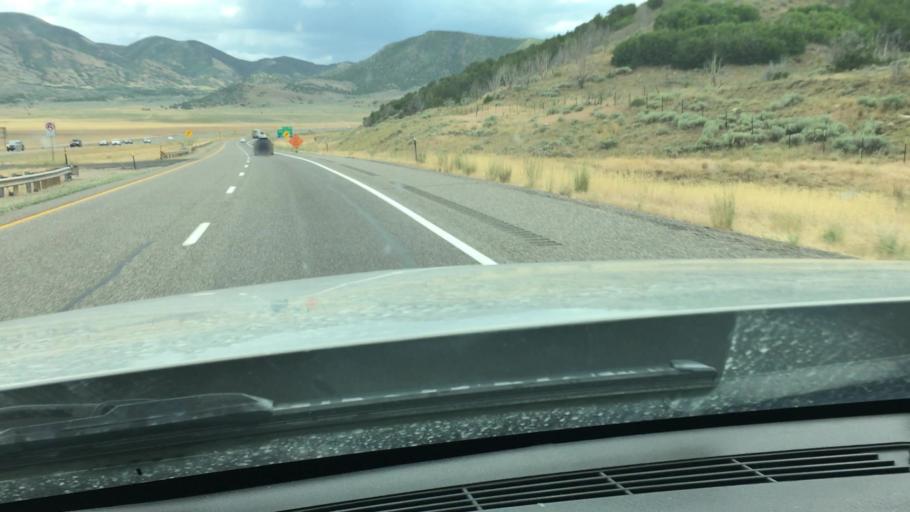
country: US
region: Utah
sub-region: Millard County
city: Fillmore
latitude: 38.6766
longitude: -112.5935
